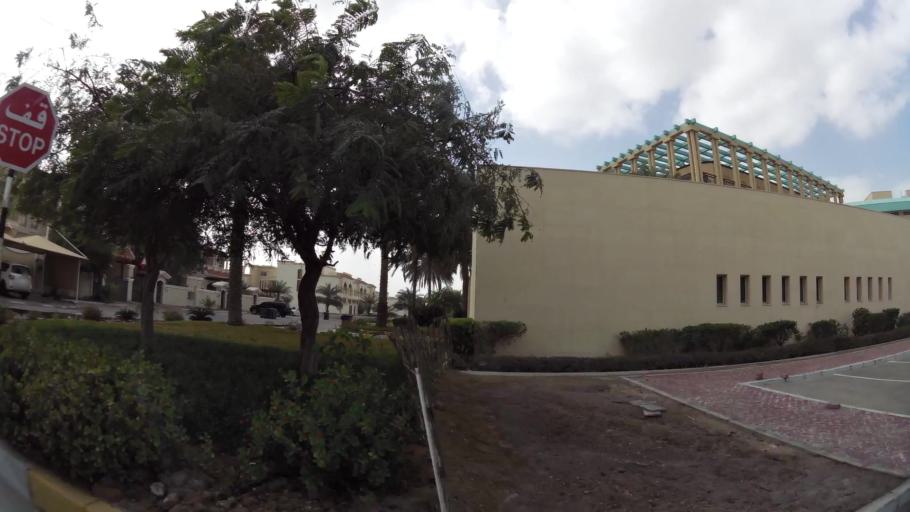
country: AE
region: Abu Dhabi
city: Abu Dhabi
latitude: 24.4088
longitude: 54.4943
